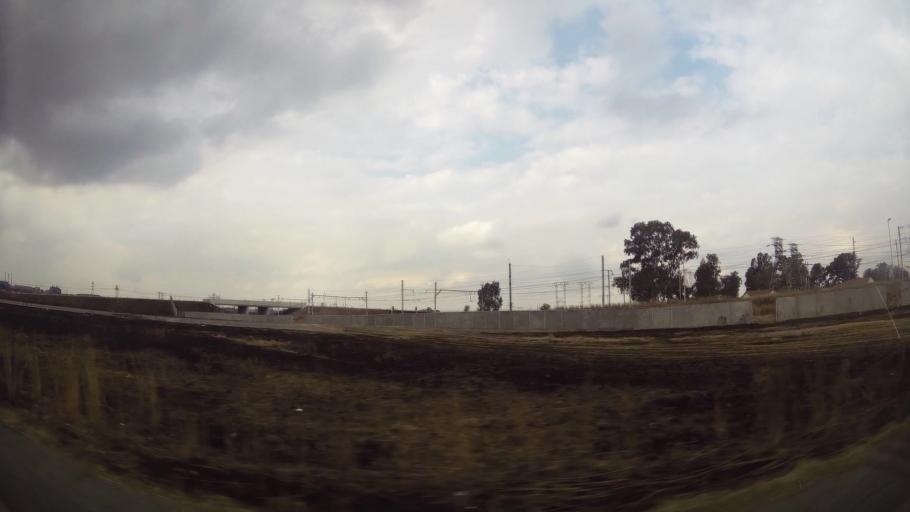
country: ZA
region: Orange Free State
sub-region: Fezile Dabi District Municipality
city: Sasolburg
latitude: -26.8434
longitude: 27.8721
